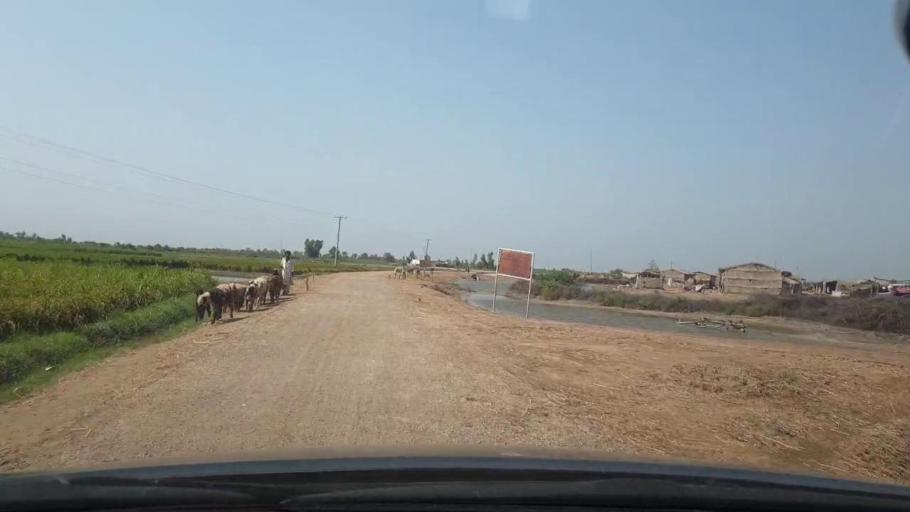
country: PK
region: Sindh
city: Tando Bago
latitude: 24.7100
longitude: 69.0843
